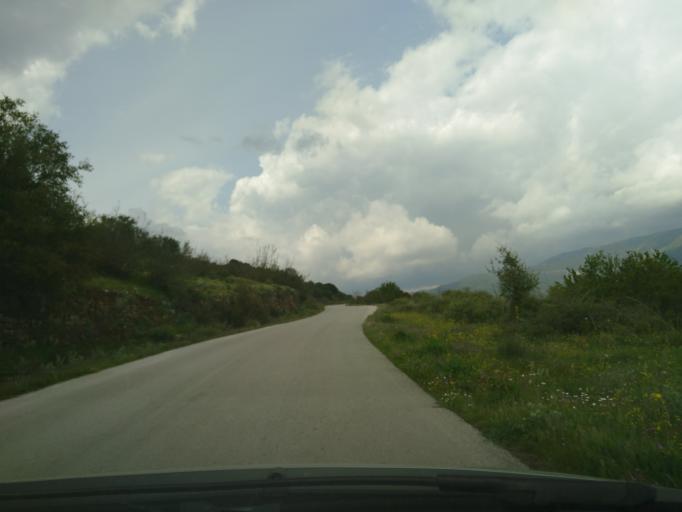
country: GR
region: Epirus
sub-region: Nomos Ioanninon
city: Asprangeloi
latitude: 39.7694
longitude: 20.6995
